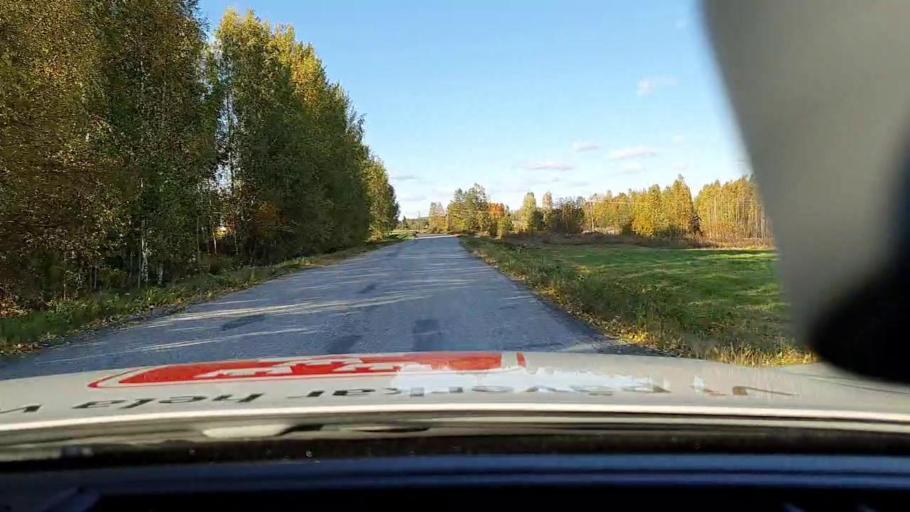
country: SE
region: Norrbotten
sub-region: Pitea Kommun
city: Norrfjarden
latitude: 65.5183
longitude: 21.4948
